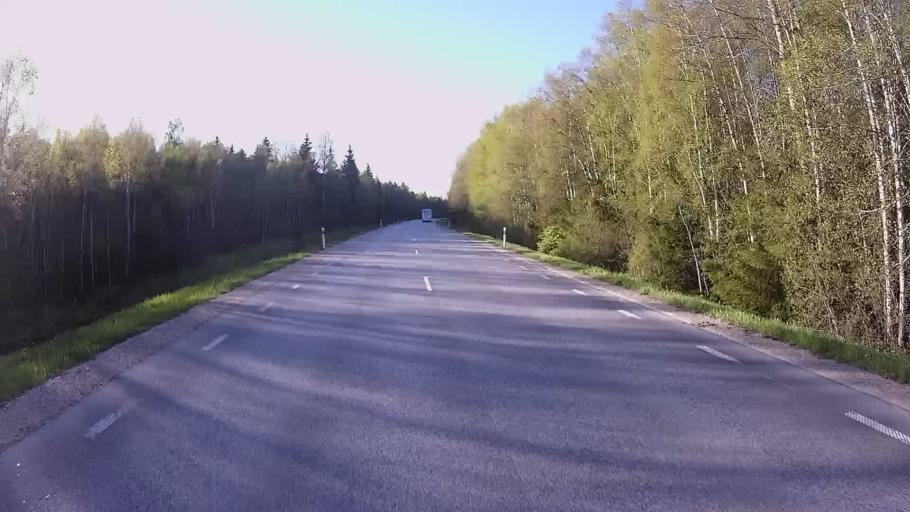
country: EE
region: Viljandimaa
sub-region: Vohma linn
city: Vohma
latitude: 58.5712
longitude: 25.5713
